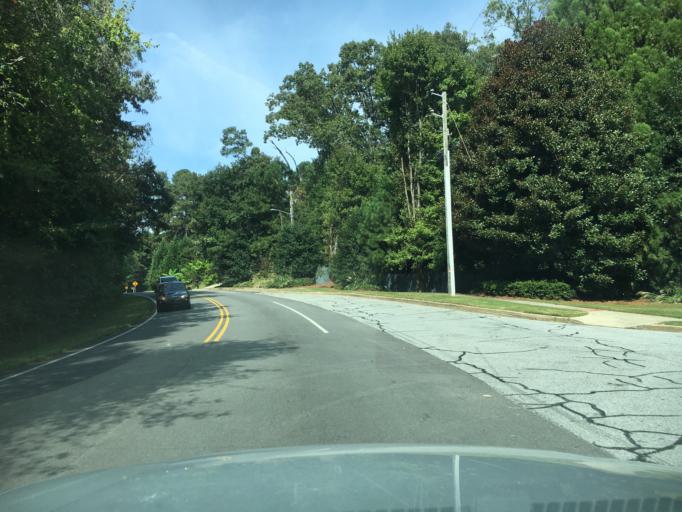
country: US
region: Georgia
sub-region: Gwinnett County
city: Duluth
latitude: 33.9708
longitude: -84.1374
